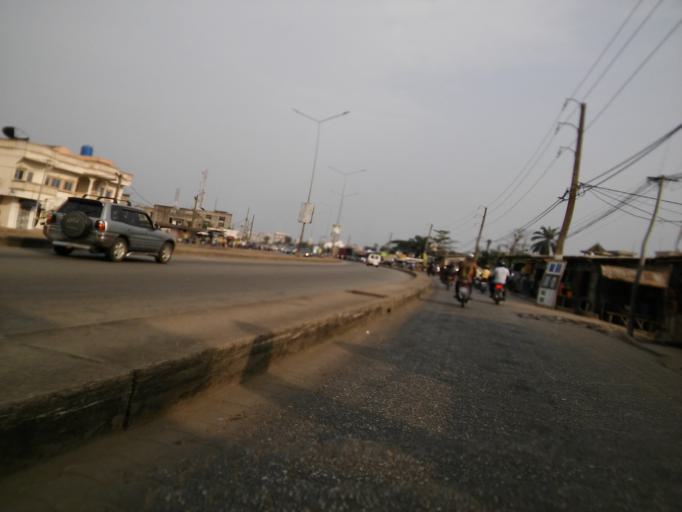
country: BJ
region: Littoral
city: Cotonou
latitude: 6.3780
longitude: 2.3810
